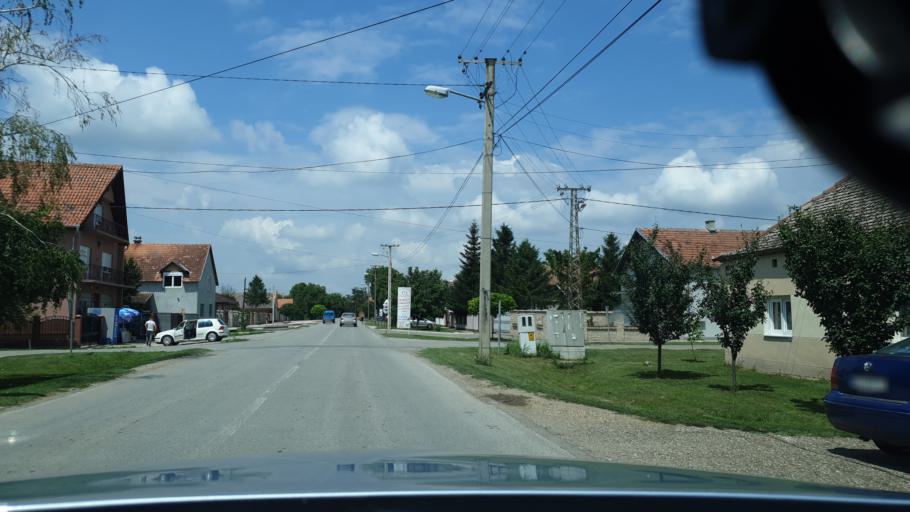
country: RS
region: Autonomna Pokrajina Vojvodina
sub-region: Juznobacki Okrug
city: Kovilj
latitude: 45.2372
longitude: 20.0290
